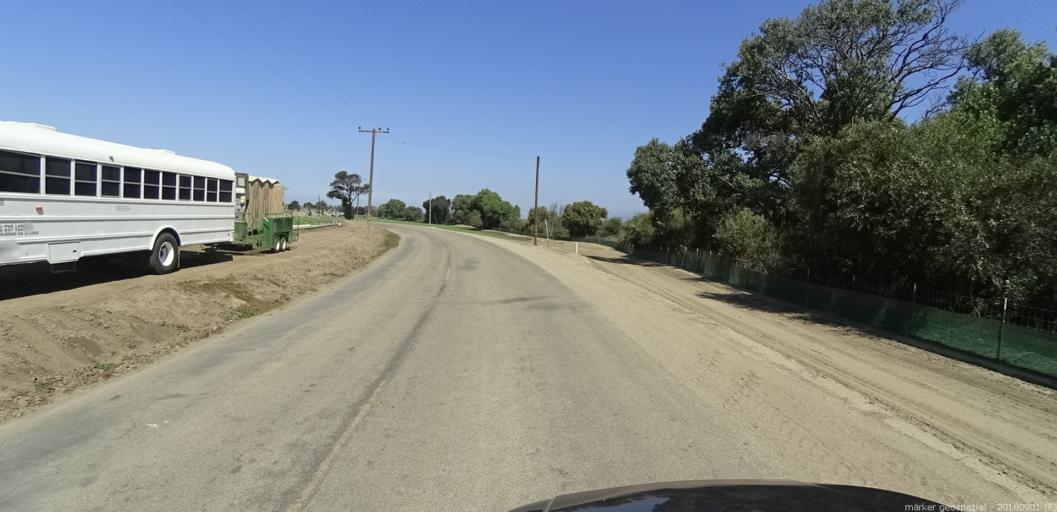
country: US
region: California
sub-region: Monterey County
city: Chualar
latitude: 36.5400
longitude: -121.5410
